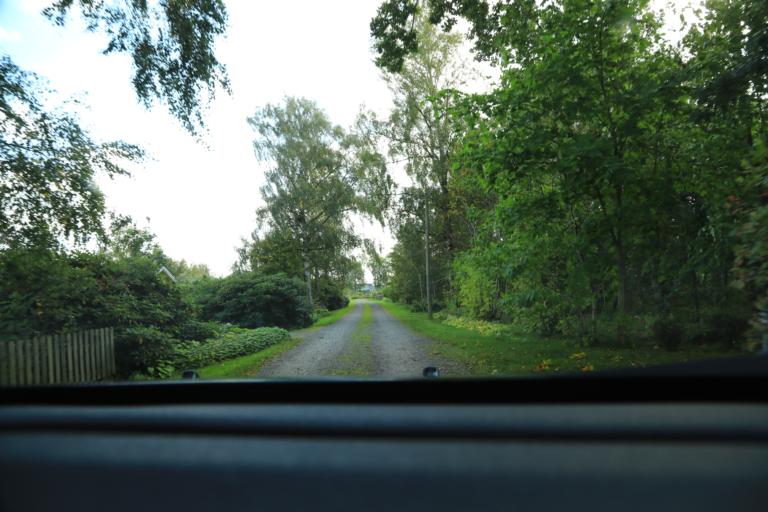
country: SE
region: Halland
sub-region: Varbergs Kommun
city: Tvaaker
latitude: 57.0105
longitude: 12.3565
